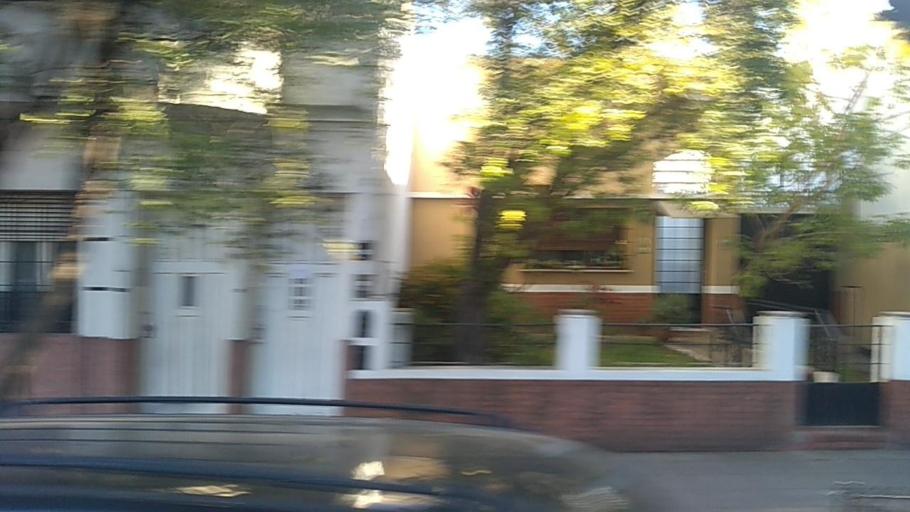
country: AR
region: Buenos Aires F.D.
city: Villa Santa Rita
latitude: -34.6238
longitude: -58.4975
